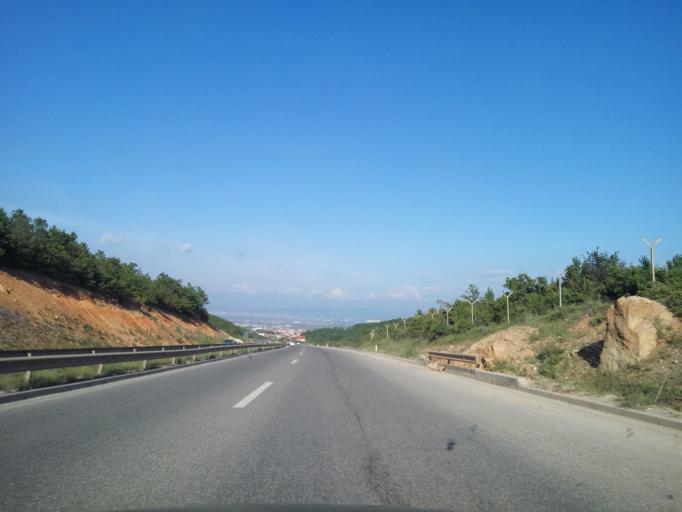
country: XK
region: Pristina
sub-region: Komuna e Gracanices
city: Glanica
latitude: 42.5961
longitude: 20.9835
